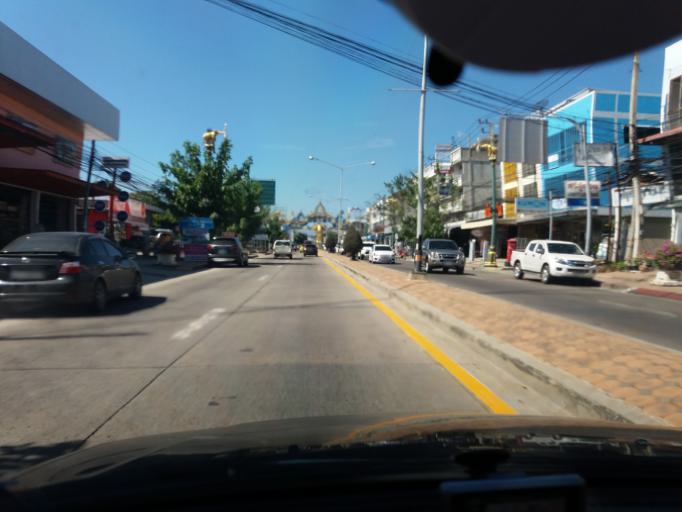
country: TH
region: Suphan Buri
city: Suphan Buri
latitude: 14.4661
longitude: 100.1269
